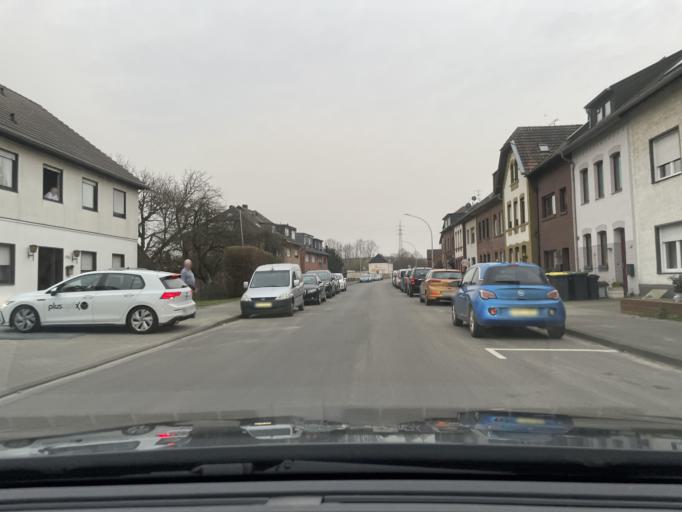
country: DE
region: North Rhine-Westphalia
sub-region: Regierungsbezirk Dusseldorf
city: Juchen
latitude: 51.0960
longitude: 6.4570
